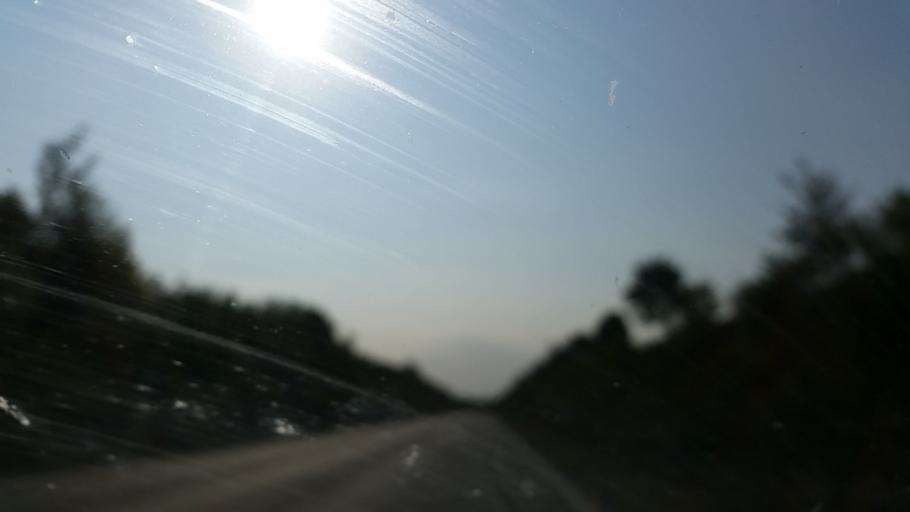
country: DE
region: Brandenburg
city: Passow
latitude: 53.1366
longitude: 14.1243
